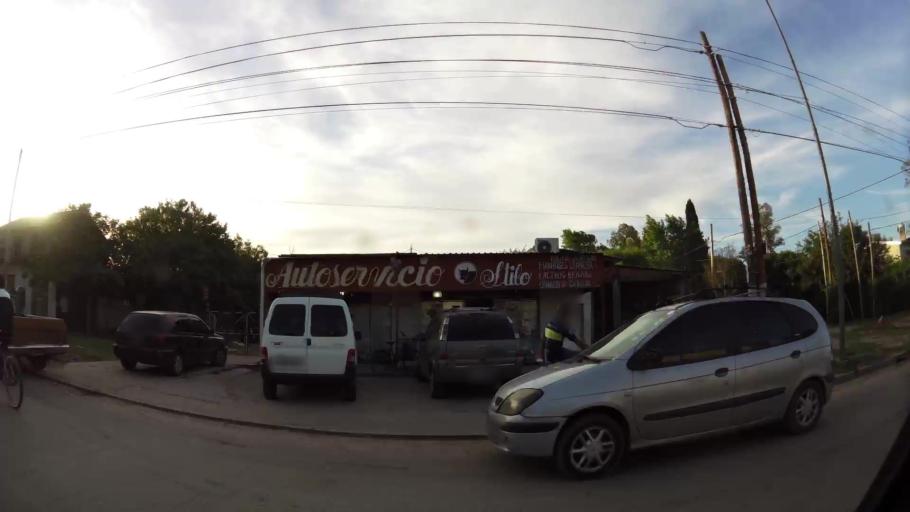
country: AR
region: Buenos Aires
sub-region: Partido de Quilmes
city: Quilmes
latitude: -34.7950
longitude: -58.1936
